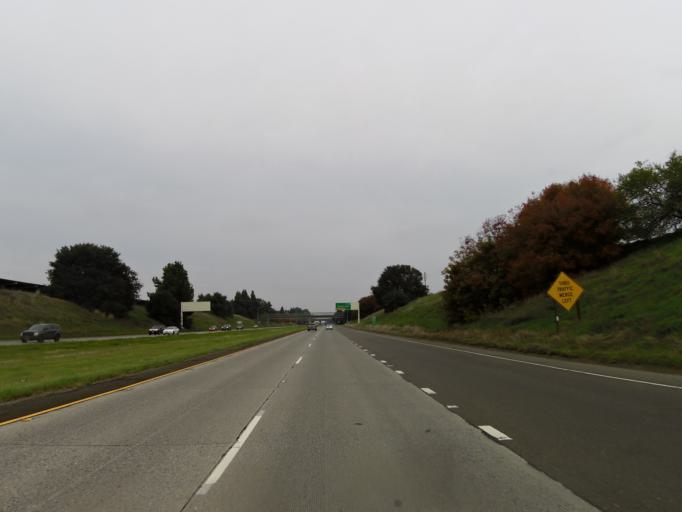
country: US
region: California
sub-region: Yolo County
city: Davis
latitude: 38.5403
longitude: -121.7682
